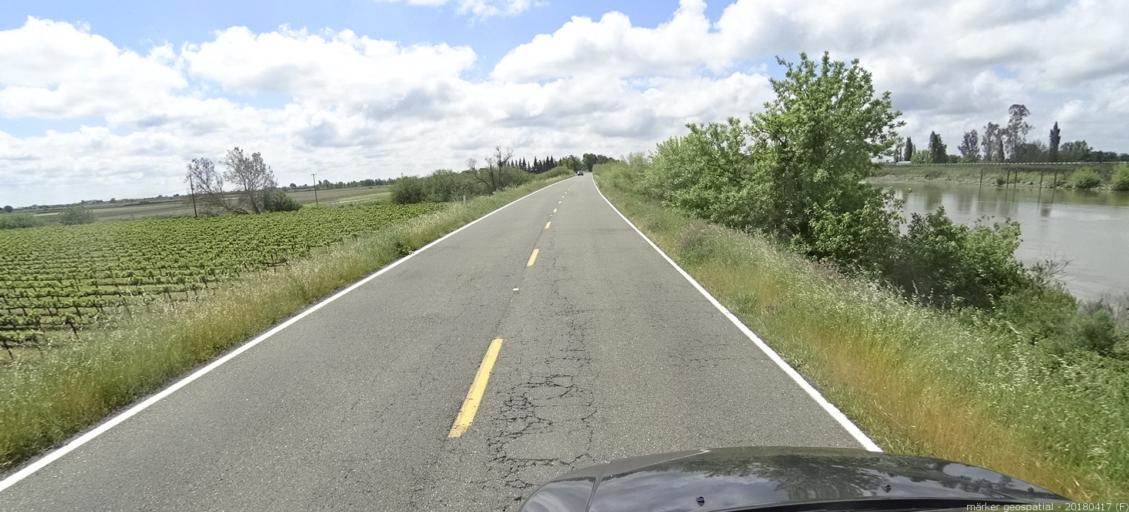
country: US
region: California
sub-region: Sacramento County
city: Walnut Grove
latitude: 38.2119
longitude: -121.5568
